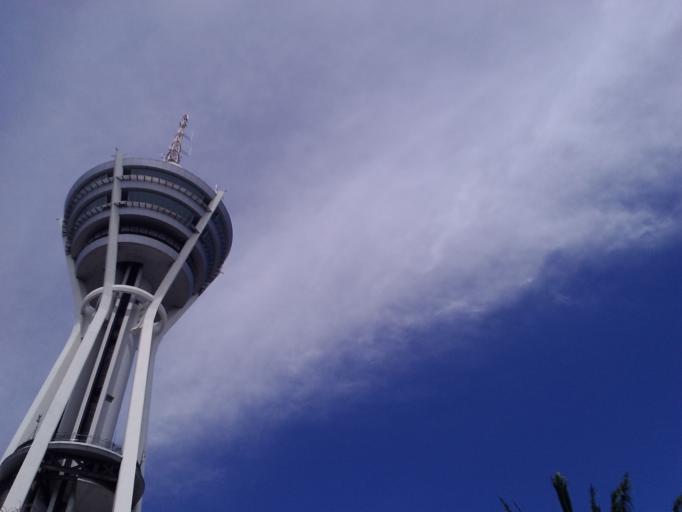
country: MY
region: Kedah
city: Alor Setar
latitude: 6.1238
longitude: 100.3676
